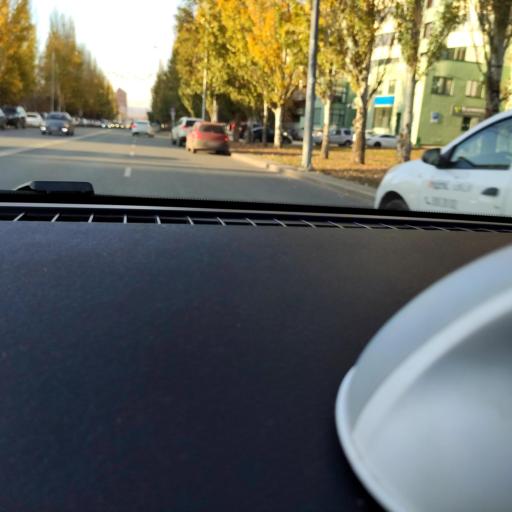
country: RU
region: Samara
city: Samara
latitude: 53.2051
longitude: 50.1392
